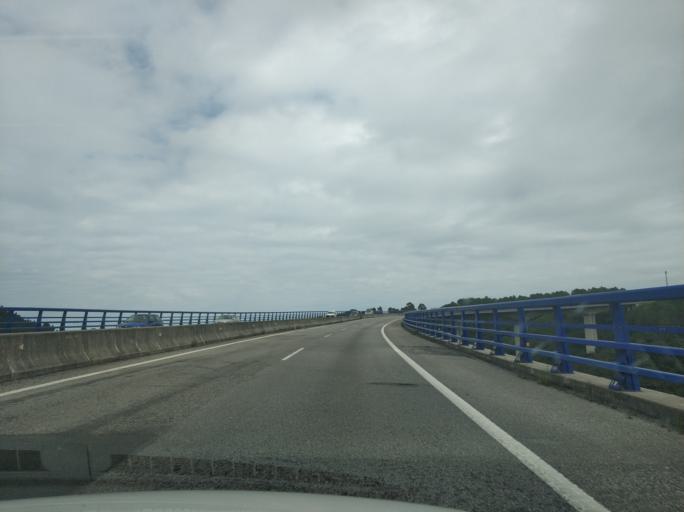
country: ES
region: Asturias
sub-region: Province of Asturias
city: Cudillero
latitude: 43.5678
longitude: -6.2266
